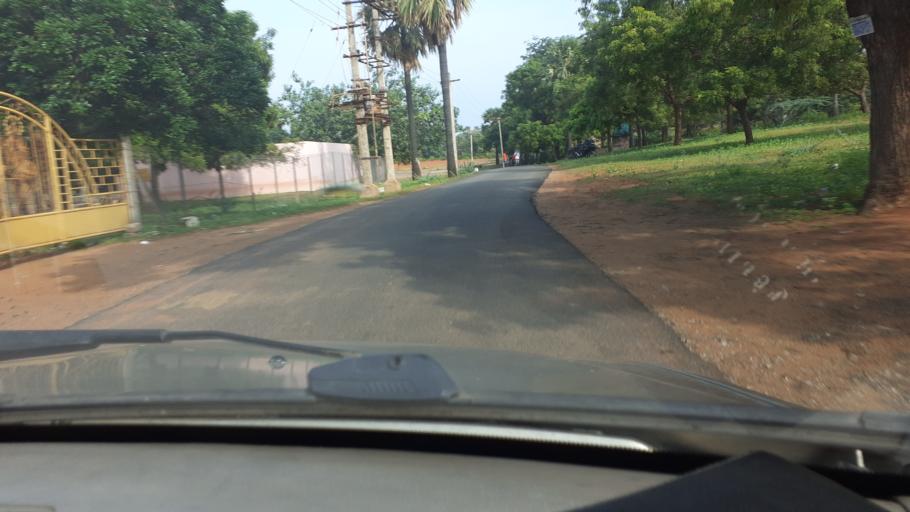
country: IN
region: Tamil Nadu
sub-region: Tirunelveli Kattabo
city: Tisaiyanvilai
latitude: 8.3360
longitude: 77.9535
